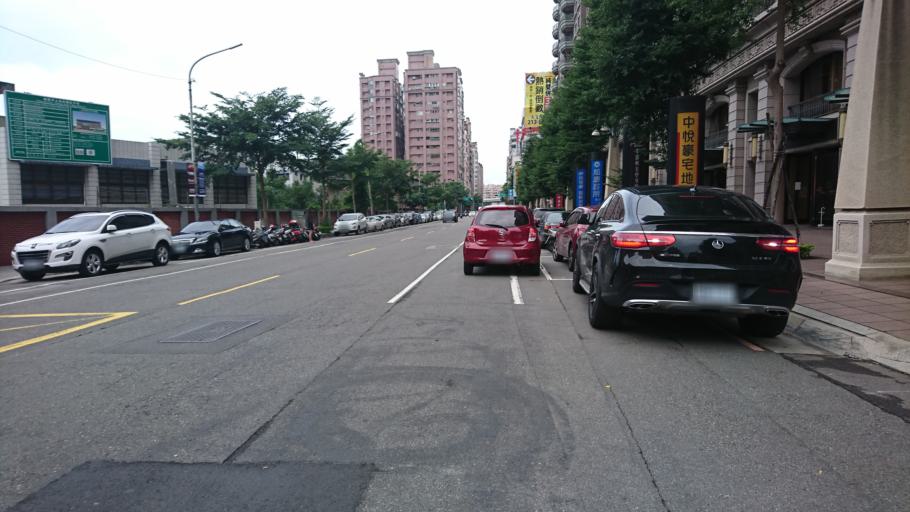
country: TW
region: Taiwan
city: Taoyuan City
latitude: 25.0537
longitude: 121.2998
